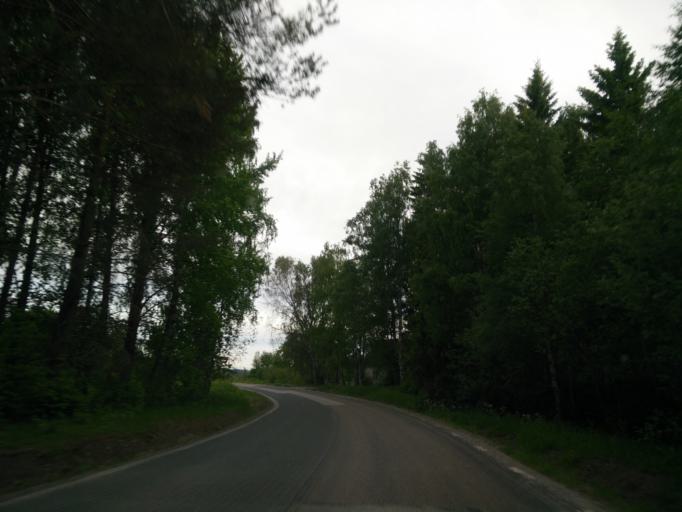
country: SE
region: Vaesternorrland
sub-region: Kramfors Kommun
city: Kramfors
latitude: 63.0351
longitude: 17.7908
